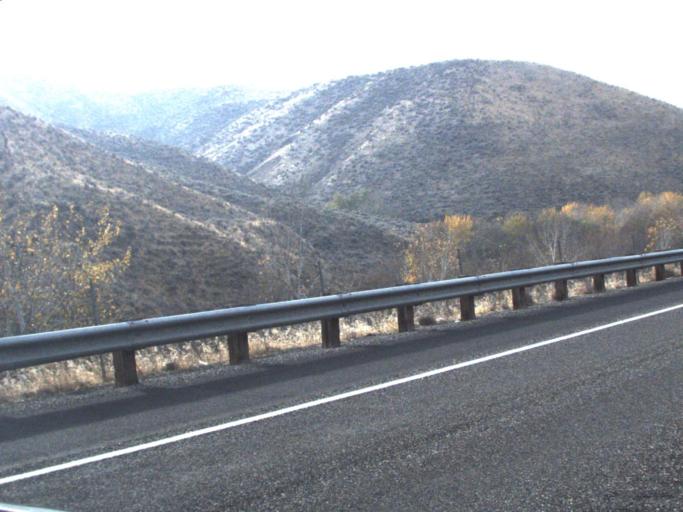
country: US
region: Washington
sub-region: Asotin County
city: Clarkston Heights-Vineland
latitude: 46.4031
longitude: -117.2422
